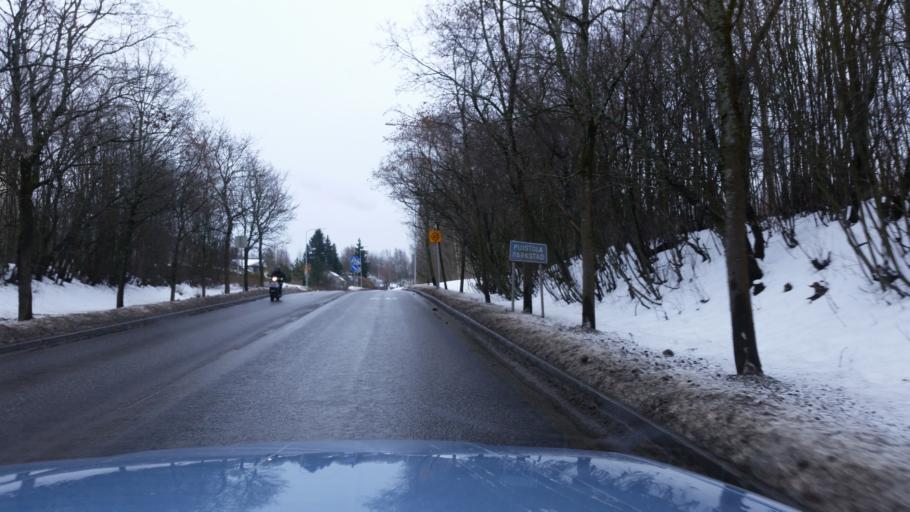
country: FI
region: Uusimaa
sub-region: Helsinki
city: Vantaa
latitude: 60.2770
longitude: 25.0381
